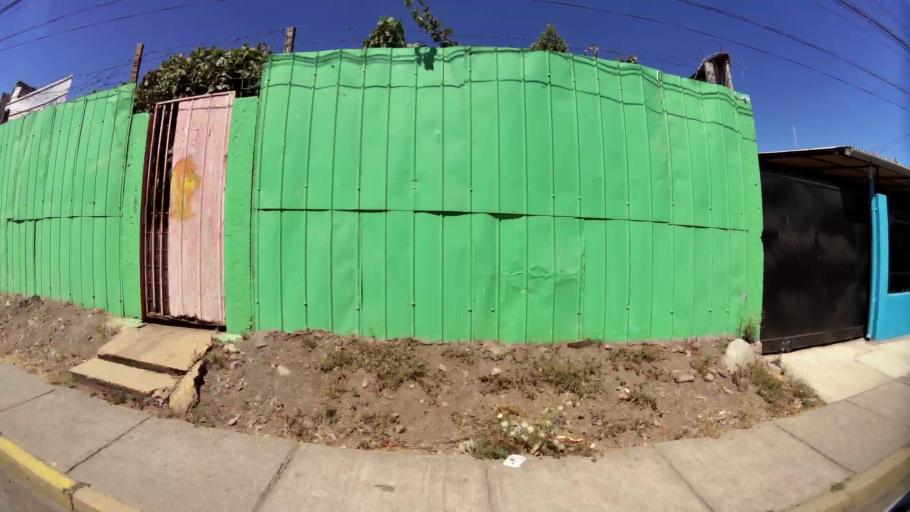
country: CL
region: O'Higgins
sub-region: Provincia de Colchagua
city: Chimbarongo
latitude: -34.5734
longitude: -70.9870
